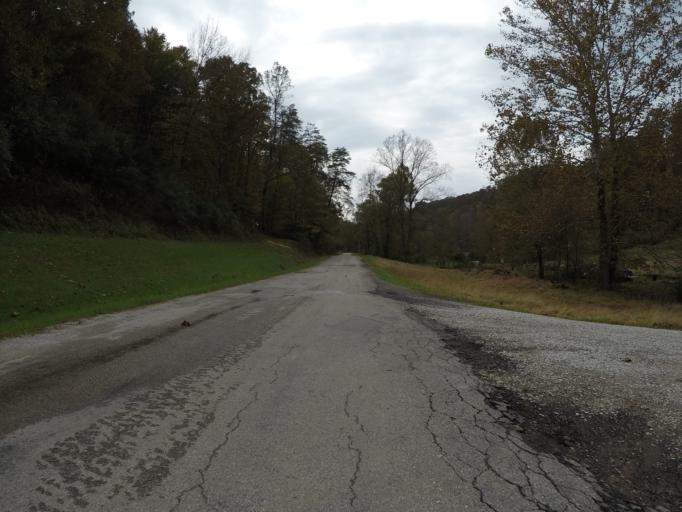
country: US
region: West Virginia
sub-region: Wayne County
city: Lavalette
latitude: 38.3517
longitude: -82.4196
